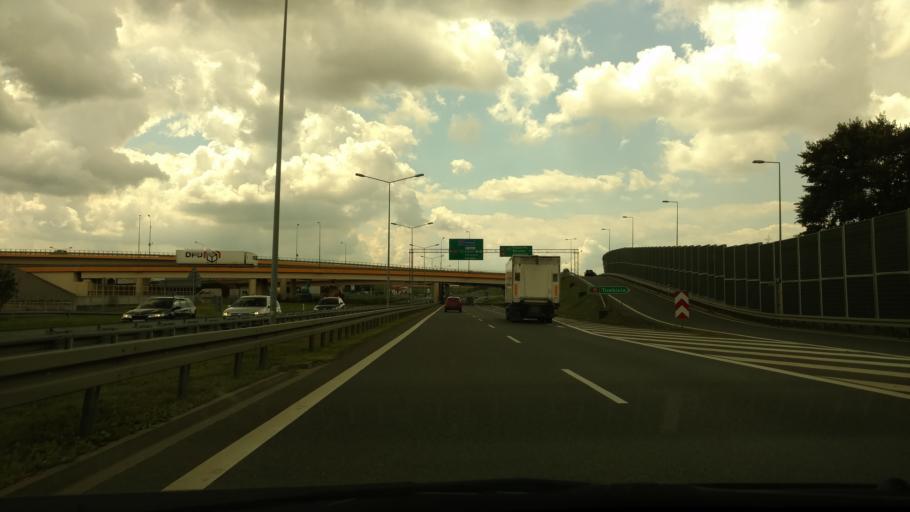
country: PL
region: Lesser Poland Voivodeship
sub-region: Powiat krakowski
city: Rzaska
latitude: 50.1090
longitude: 19.8421
